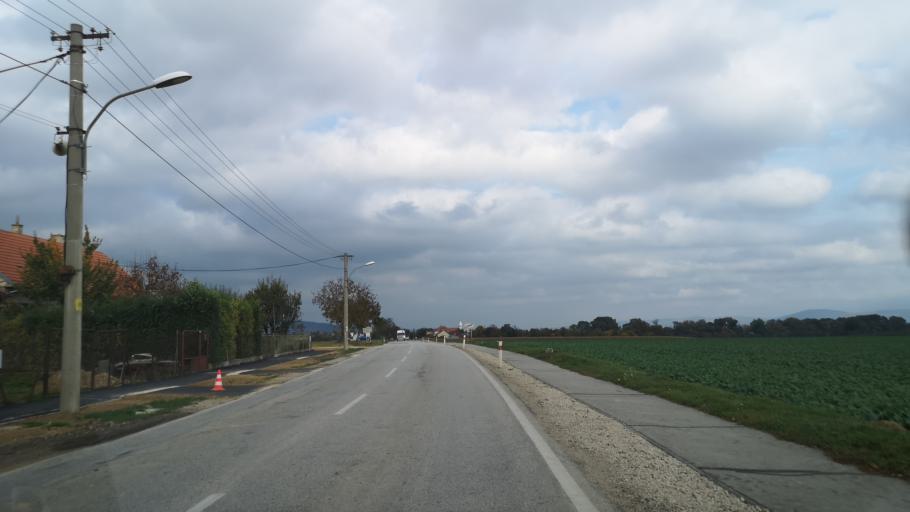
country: SK
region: Nitriansky
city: Cachtice
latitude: 48.6809
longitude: 17.7751
